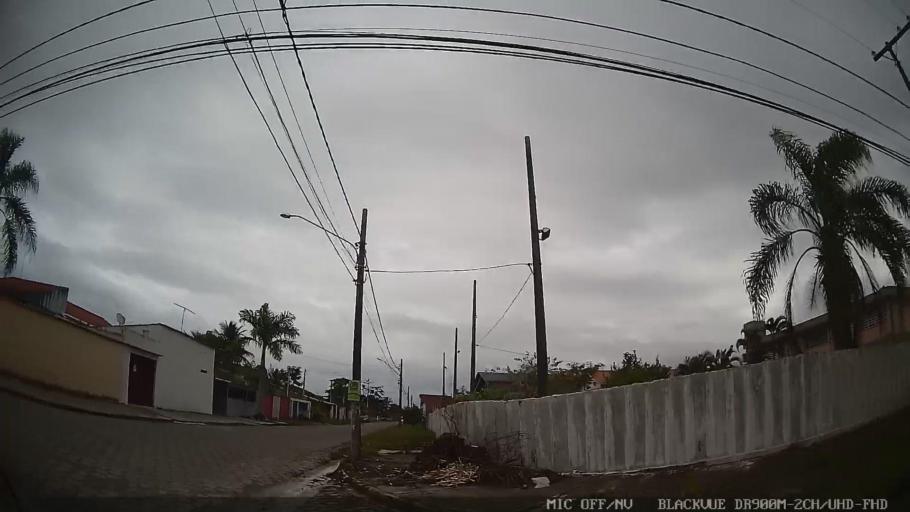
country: BR
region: Sao Paulo
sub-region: Itanhaem
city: Itanhaem
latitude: -24.2390
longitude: -46.8932
